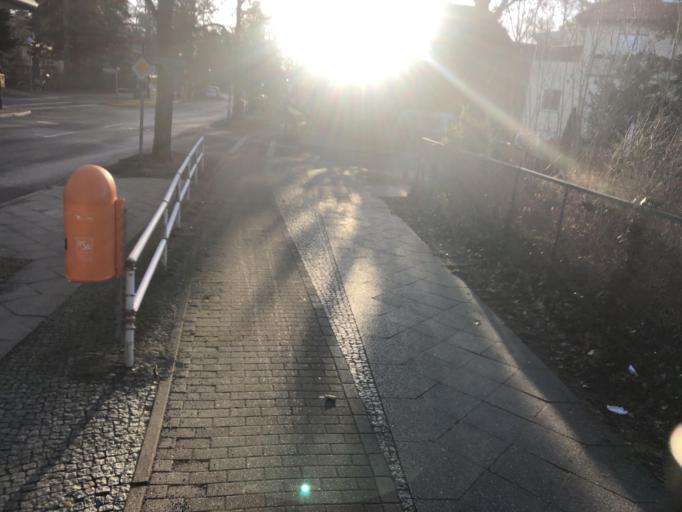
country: DE
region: Berlin
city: Frohnau
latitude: 52.6310
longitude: 13.2723
